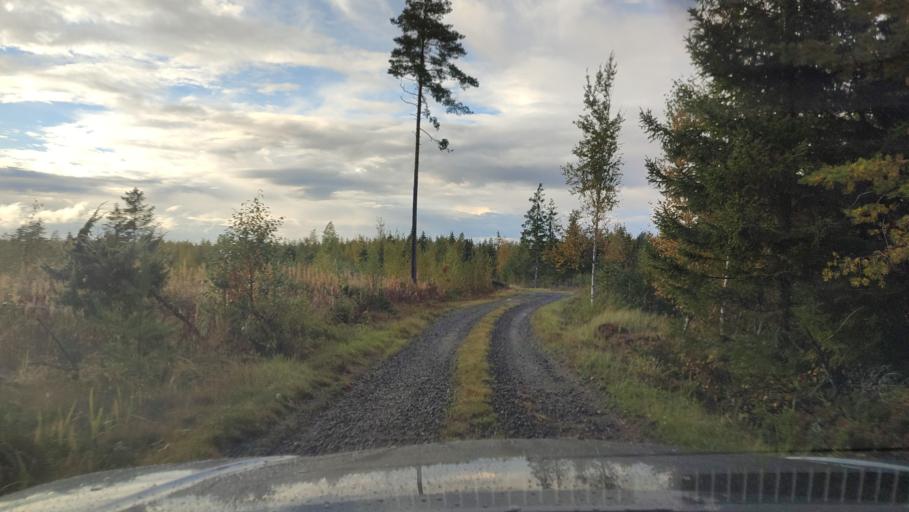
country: FI
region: Ostrobothnia
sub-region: Sydosterbotten
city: Kristinestad
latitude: 62.3027
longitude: 21.5066
